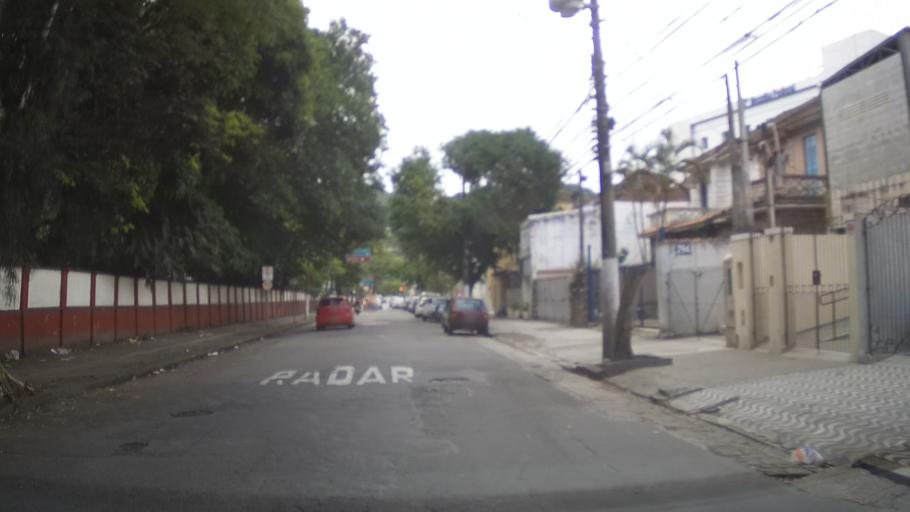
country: BR
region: Sao Paulo
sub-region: Santos
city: Santos
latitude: -23.9487
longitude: -46.3353
